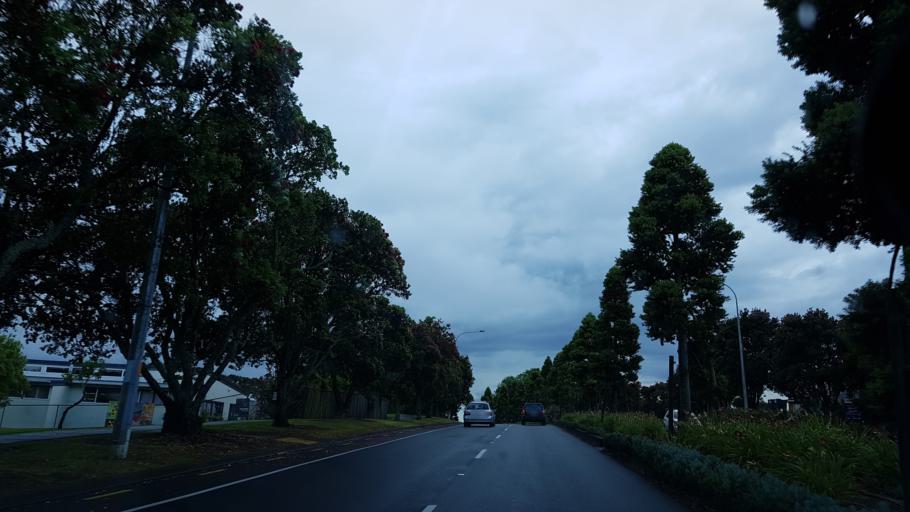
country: NZ
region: Auckland
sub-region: Auckland
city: North Shore
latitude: -36.7791
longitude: 174.7224
